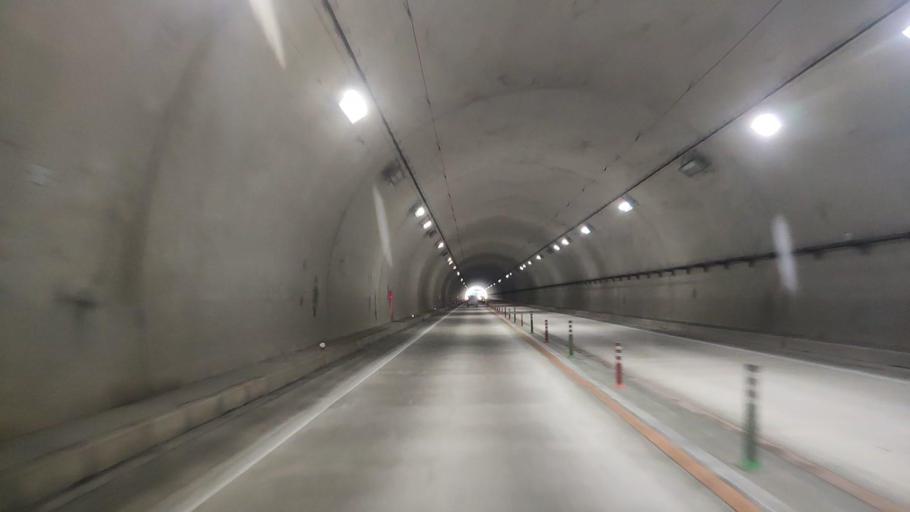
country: JP
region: Wakayama
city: Shingu
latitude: 33.6249
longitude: 135.9203
